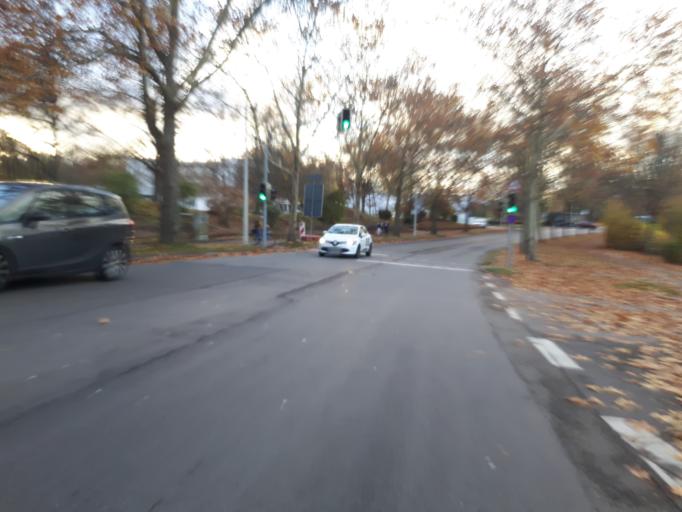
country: DE
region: Baden-Wuerttemberg
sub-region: Regierungsbezirk Stuttgart
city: Flein
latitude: 49.1209
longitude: 9.2149
